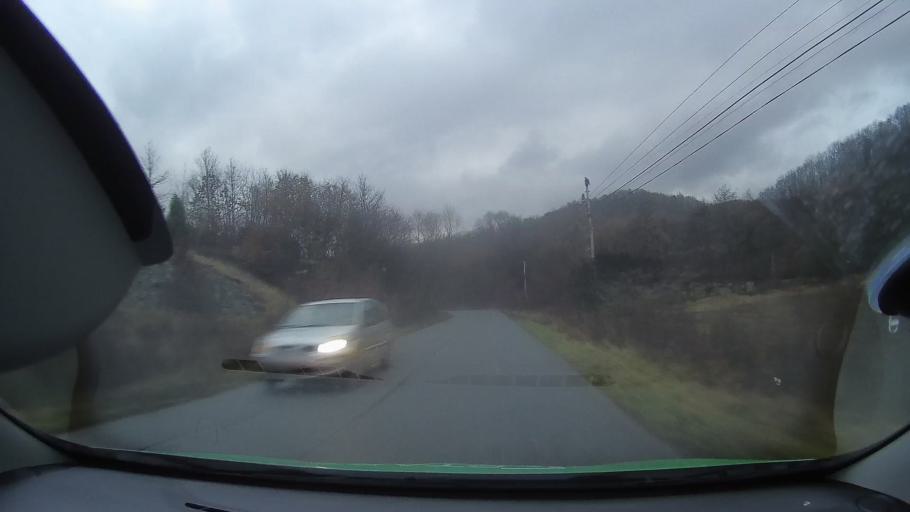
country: RO
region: Hunedoara
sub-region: Comuna Baia de Cris
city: Baia de Cris
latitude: 46.1940
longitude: 22.7175
